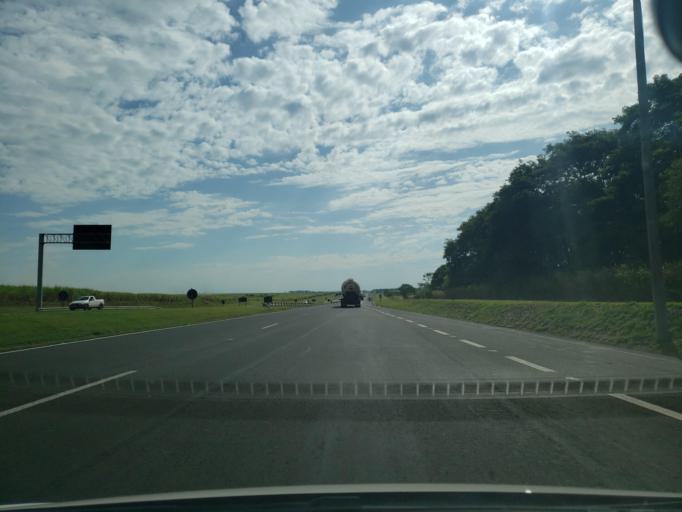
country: BR
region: Sao Paulo
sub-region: Promissao
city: Promissao
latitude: -21.6211
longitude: -49.8540
